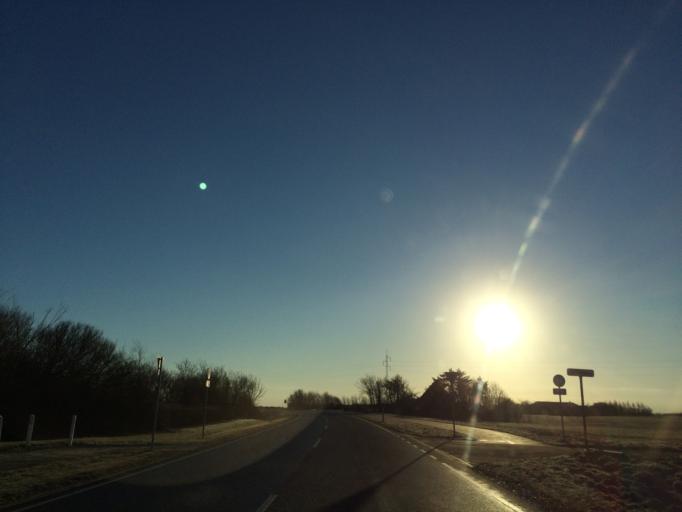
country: DK
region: Central Jutland
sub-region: Lemvig Kommune
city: Lemvig
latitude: 56.5297
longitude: 8.3717
